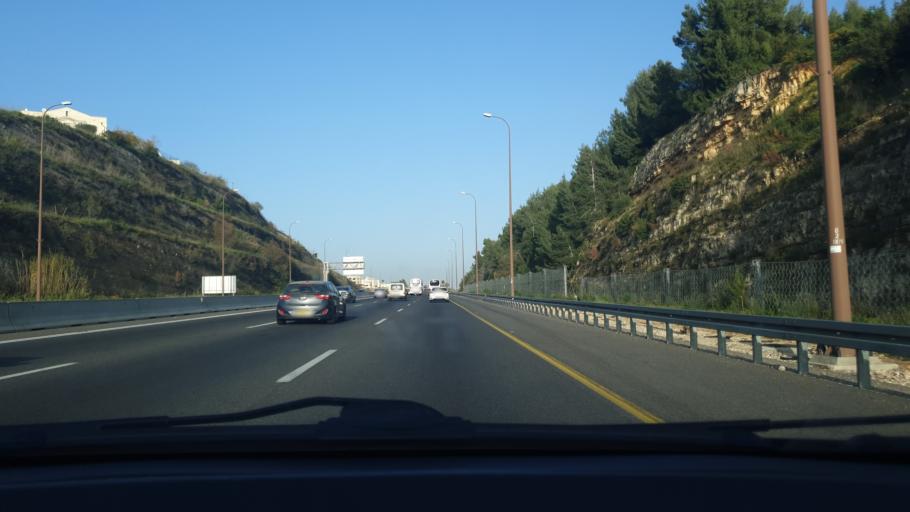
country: IL
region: Jerusalem
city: Abu Ghaush
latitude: 31.8013
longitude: 35.1027
